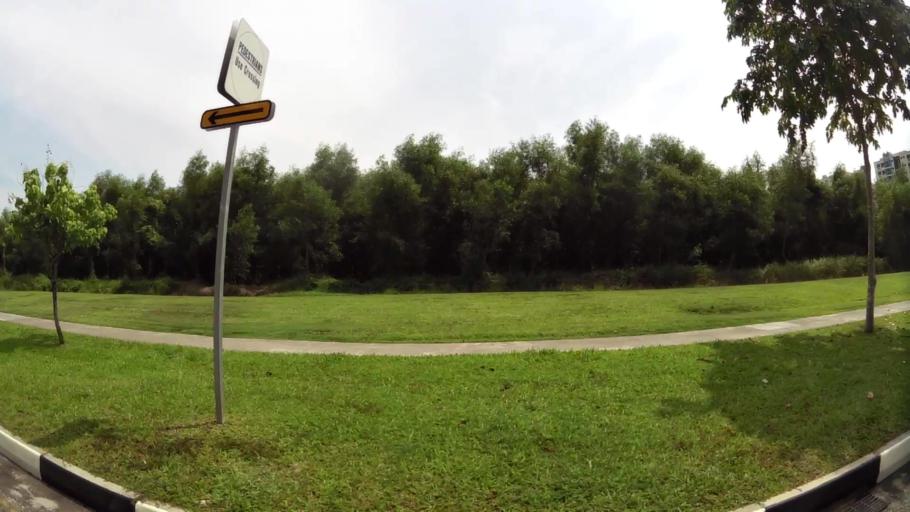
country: MY
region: Johor
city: Kampung Pasir Gudang Baru
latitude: 1.3759
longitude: 103.9617
